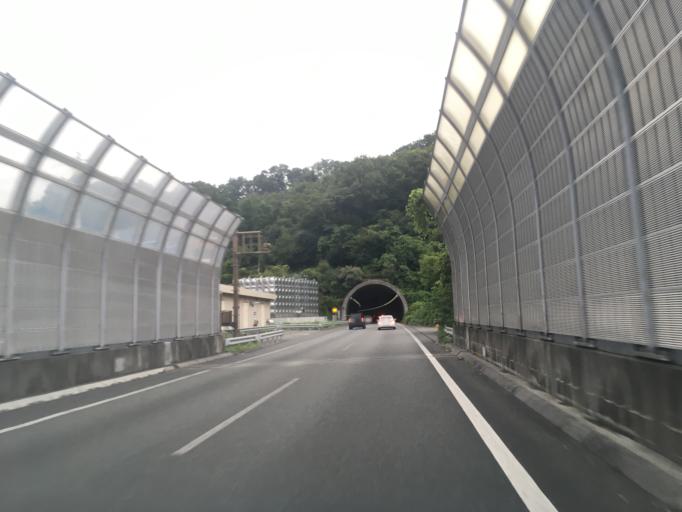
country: JP
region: Tokyo
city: Itsukaichi
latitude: 35.6989
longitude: 139.2704
